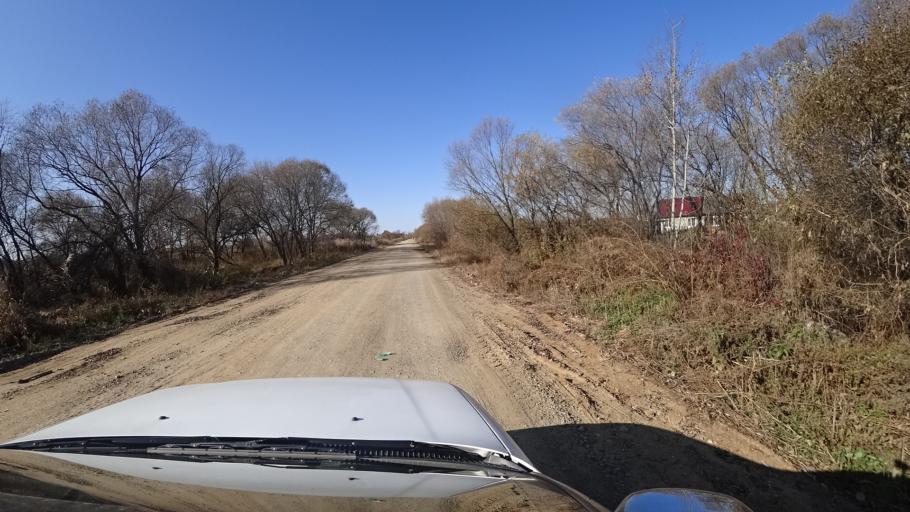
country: RU
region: Primorskiy
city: Dal'nerechensk
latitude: 45.9078
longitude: 133.8082
